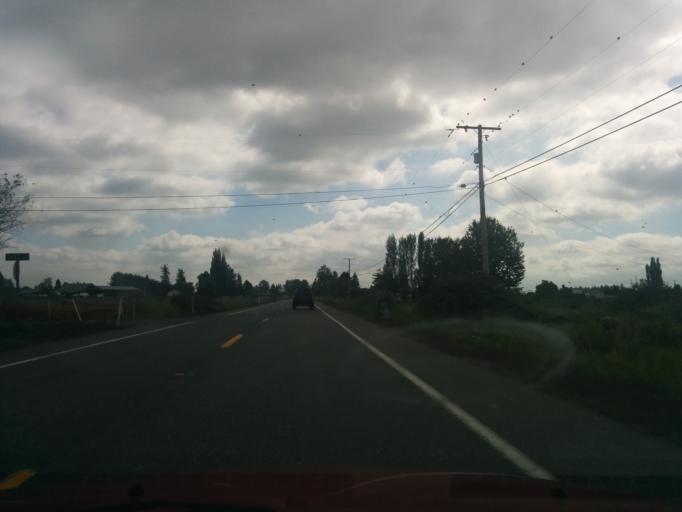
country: US
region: Washington
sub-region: Skagit County
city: Burlington
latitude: 48.5702
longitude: -122.4222
